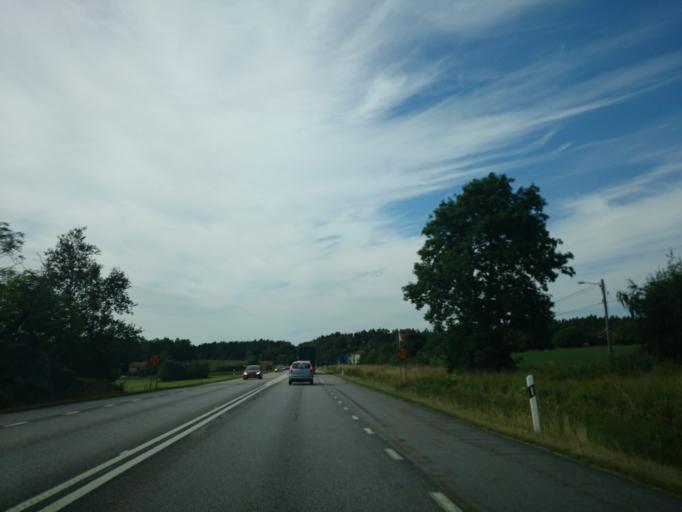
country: SE
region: Kalmar
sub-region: Vasterviks Kommun
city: Ankarsrum
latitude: 57.7124
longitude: 16.4496
